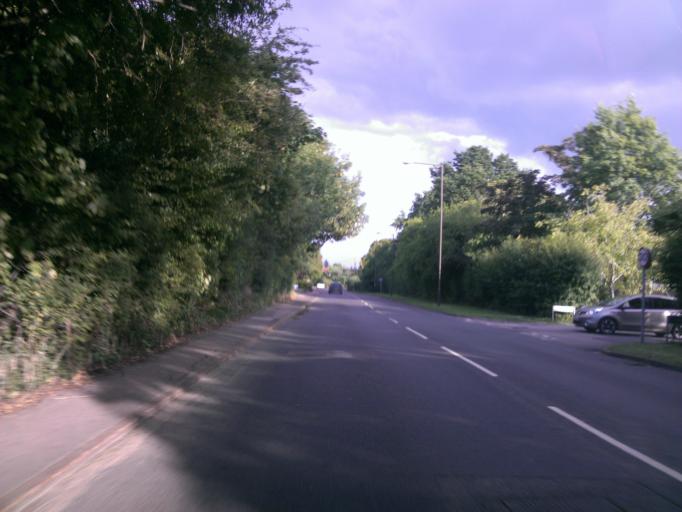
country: GB
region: England
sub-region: Kent
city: Tonbridge
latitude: 51.2114
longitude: 0.2534
